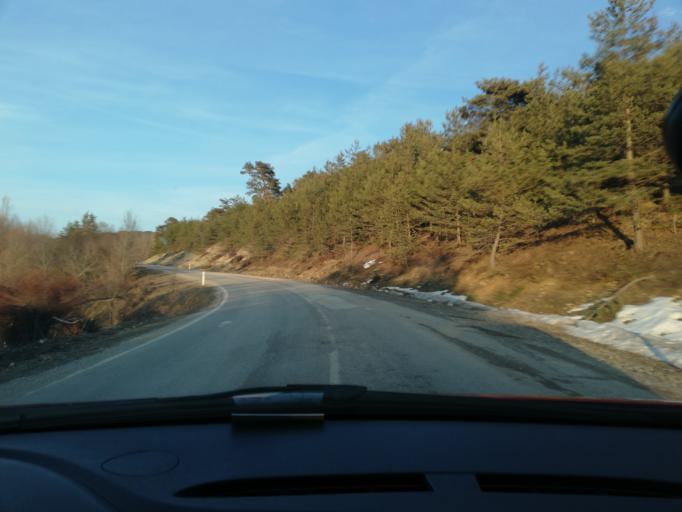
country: TR
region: Kastamonu
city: Agli
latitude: 41.7030
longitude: 33.6466
